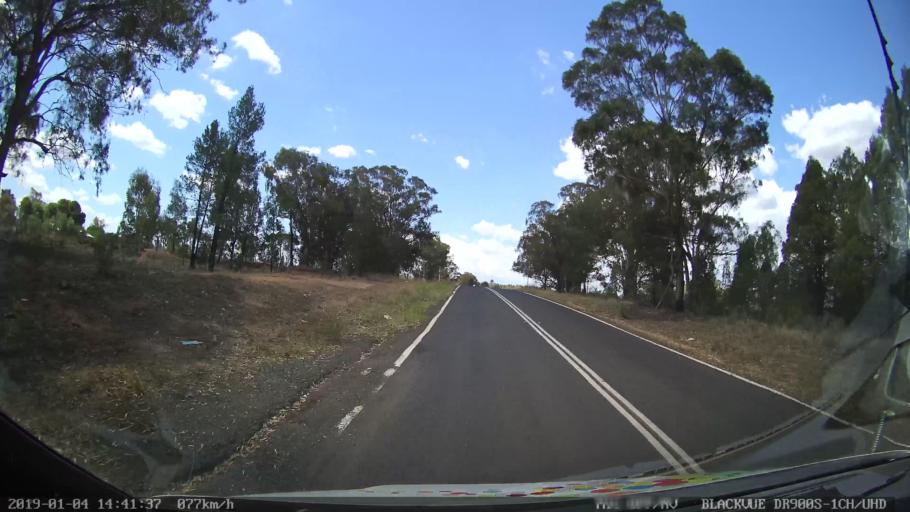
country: AU
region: New South Wales
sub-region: Dubbo Municipality
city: Dubbo
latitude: -32.1370
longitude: 148.6367
